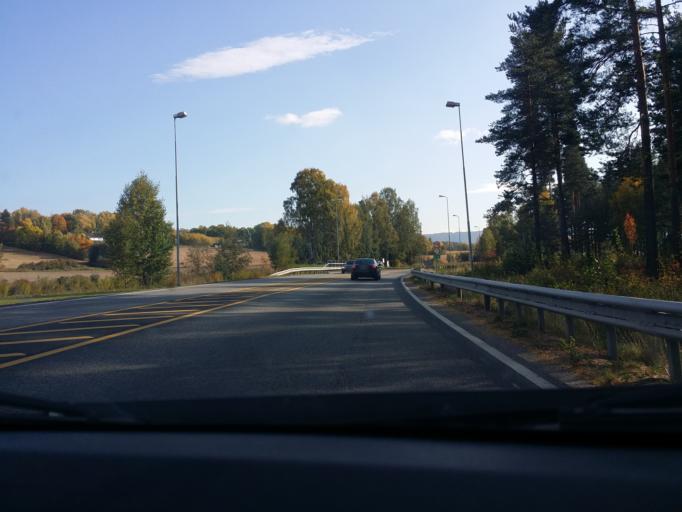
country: NO
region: Buskerud
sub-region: Ringerike
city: Honefoss
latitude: 60.1454
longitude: 10.2583
